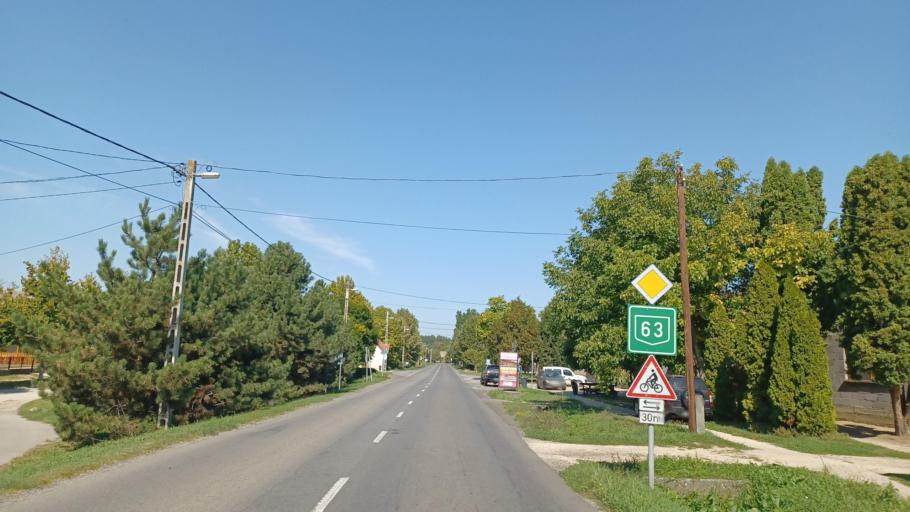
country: HU
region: Tolna
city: Nagydorog
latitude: 46.6757
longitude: 18.6676
